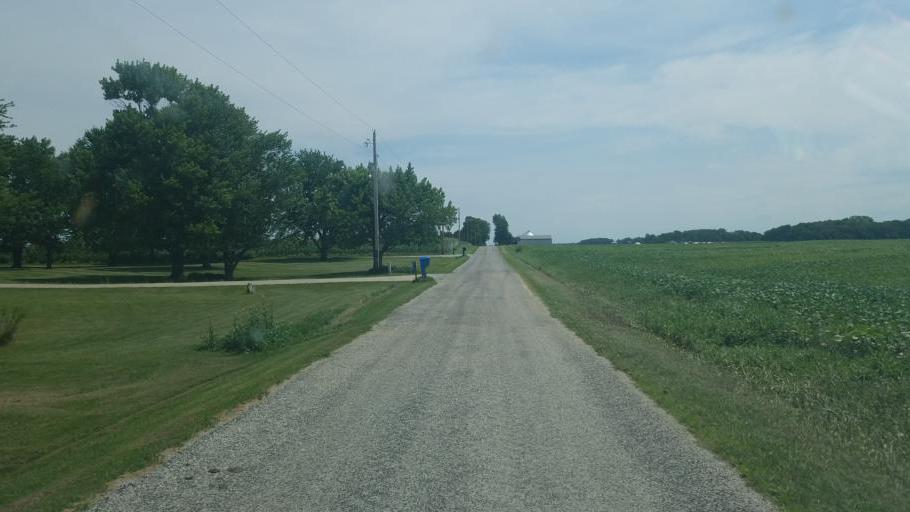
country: US
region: Ohio
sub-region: Crawford County
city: Bucyrus
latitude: 40.8740
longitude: -82.9356
